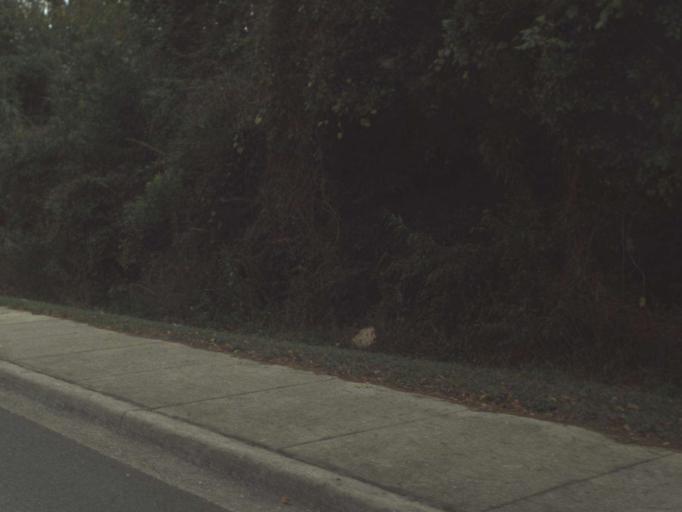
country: US
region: Florida
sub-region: Leon County
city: Tallahassee
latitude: 30.5154
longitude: -84.2418
